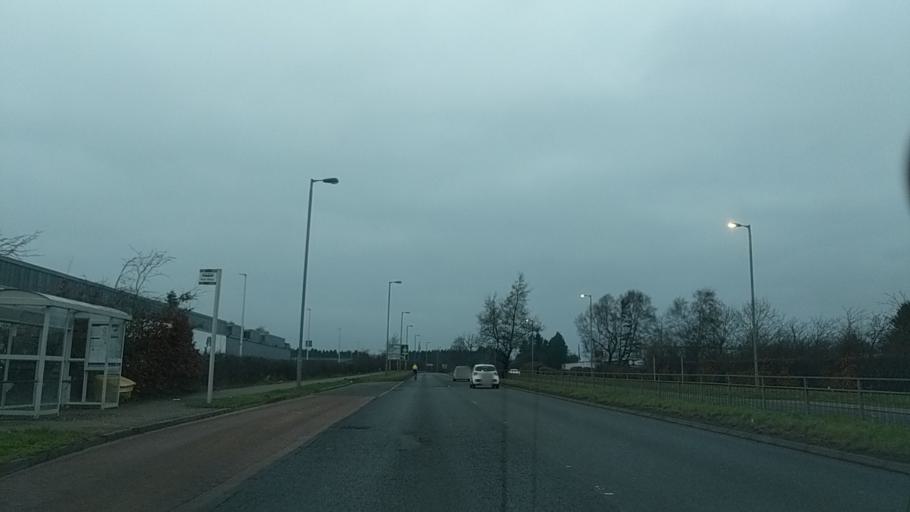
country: GB
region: Scotland
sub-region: Glasgow City
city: Carmunnock
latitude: 55.7655
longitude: -4.2122
